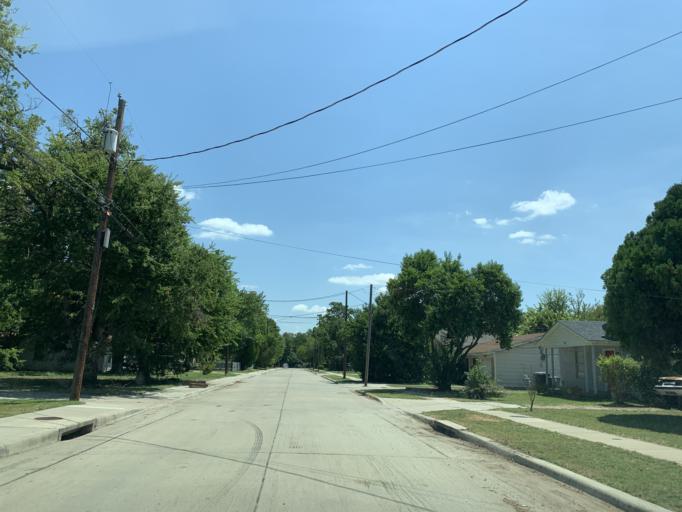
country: US
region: Texas
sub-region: Dallas County
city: Hutchins
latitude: 32.6883
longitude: -96.7752
